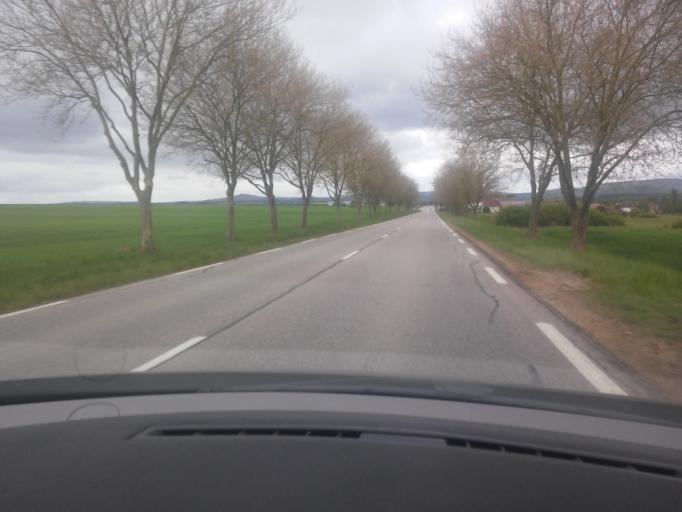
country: FR
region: Lorraine
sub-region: Departement de la Moselle
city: Verny
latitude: 48.9602
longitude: 6.1972
